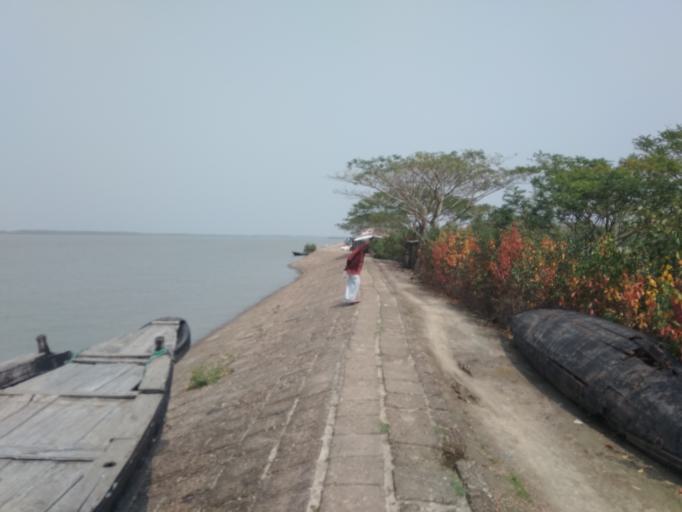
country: IN
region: West Bengal
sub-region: North 24 Parganas
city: Gosaba
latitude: 22.2541
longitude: 89.2506
